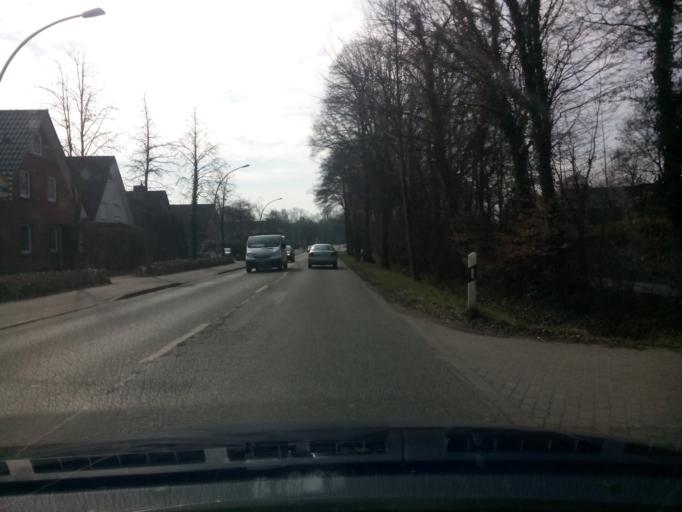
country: DE
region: Lower Saxony
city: Osterholz-Scharmbeck
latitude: 53.2201
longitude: 8.7821
